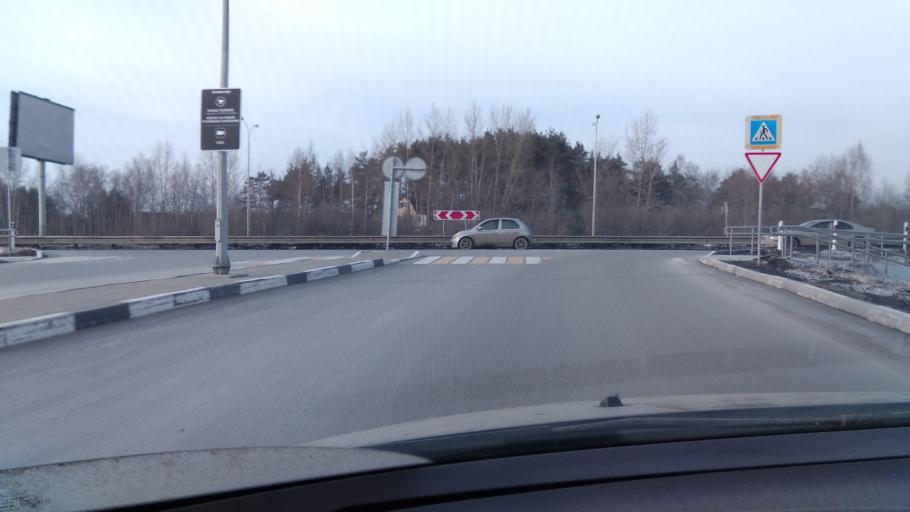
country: RU
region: Sverdlovsk
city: Shirokaya Rechka
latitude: 56.8256
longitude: 60.5046
